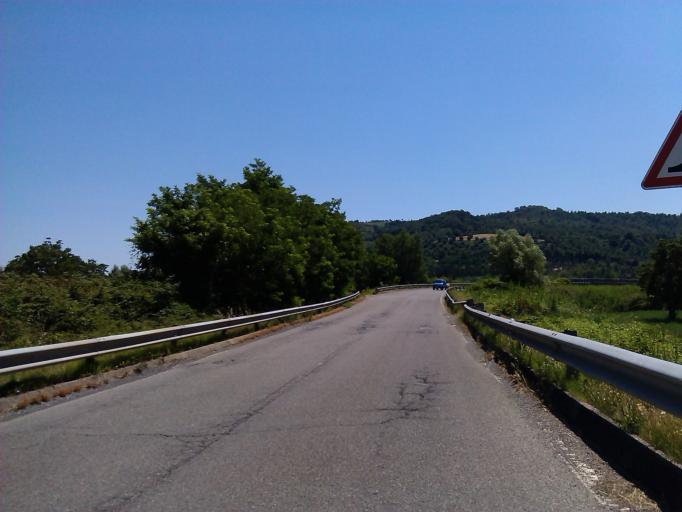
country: IT
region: Umbria
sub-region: Provincia di Terni
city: Fabro Scalo
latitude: 42.8692
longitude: 12.0447
